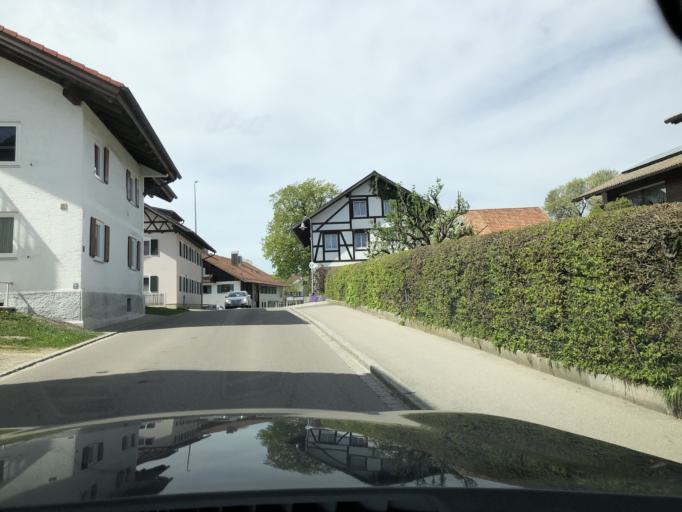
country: DE
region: Bavaria
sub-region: Swabia
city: Seeg
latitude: 47.6548
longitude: 10.6105
